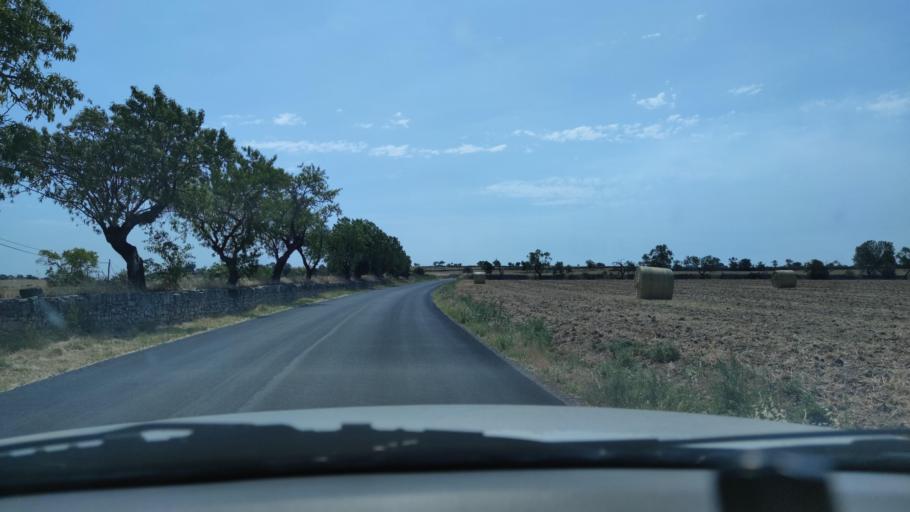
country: ES
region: Catalonia
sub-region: Provincia de Lleida
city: Ivorra
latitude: 41.7787
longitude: 1.3133
